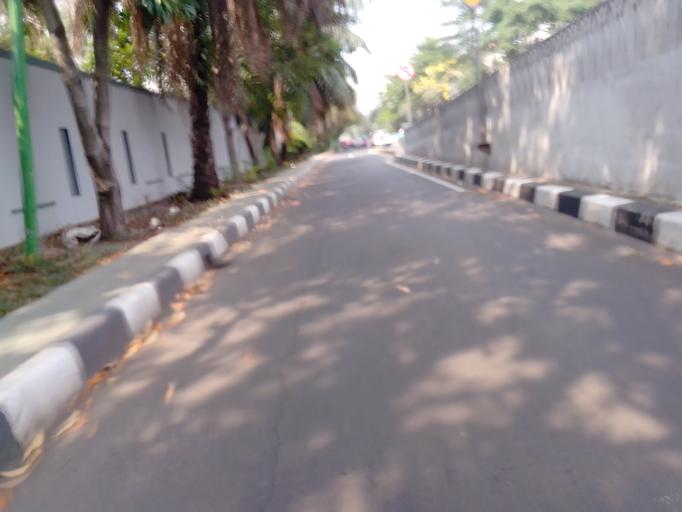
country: ID
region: Jakarta Raya
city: Jakarta
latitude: -6.2235
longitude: 106.7918
